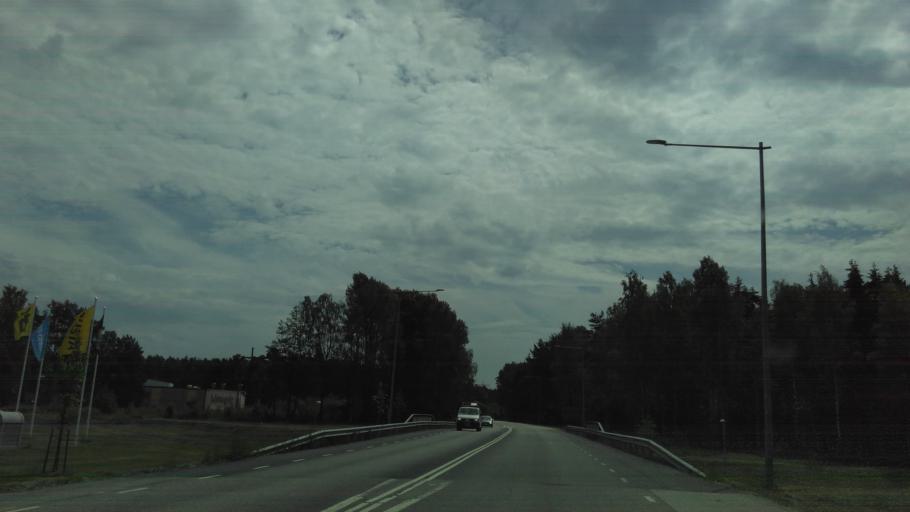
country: SE
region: Vaestra Goetaland
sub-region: Lidkopings Kommun
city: Lidkoping
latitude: 58.4926
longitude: 13.1823
